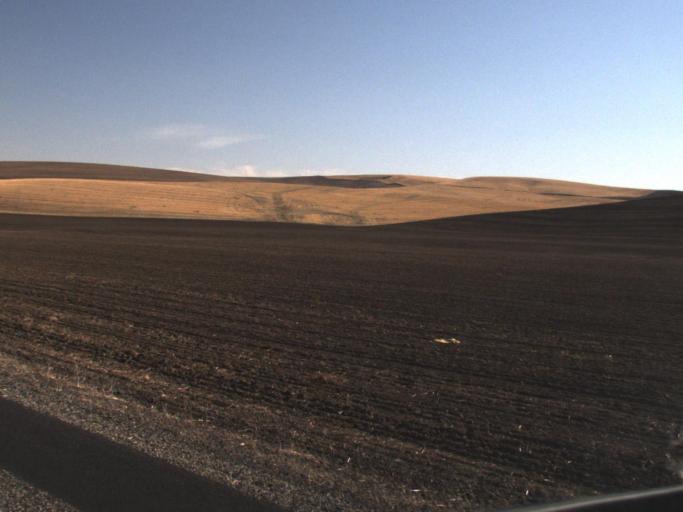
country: US
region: Washington
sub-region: Walla Walla County
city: Waitsburg
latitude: 46.2666
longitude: -118.2161
